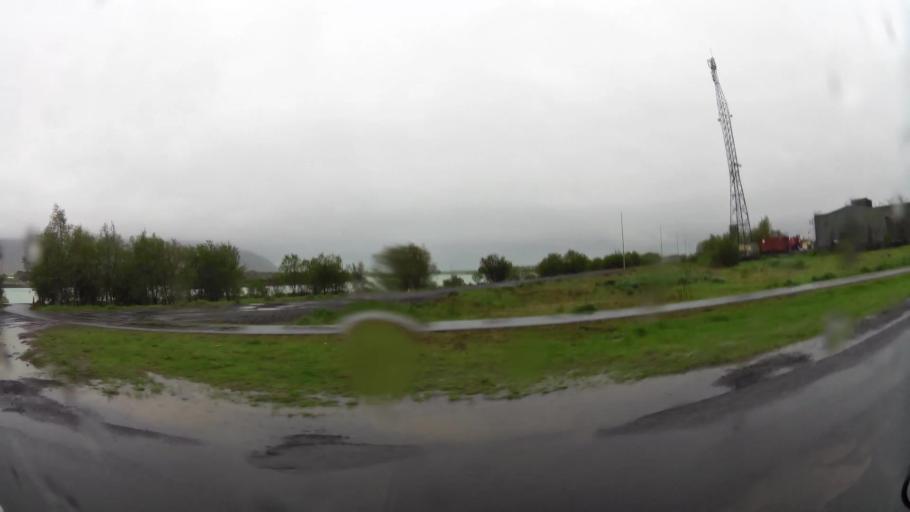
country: IS
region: South
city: Selfoss
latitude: 63.9387
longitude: -20.9926
